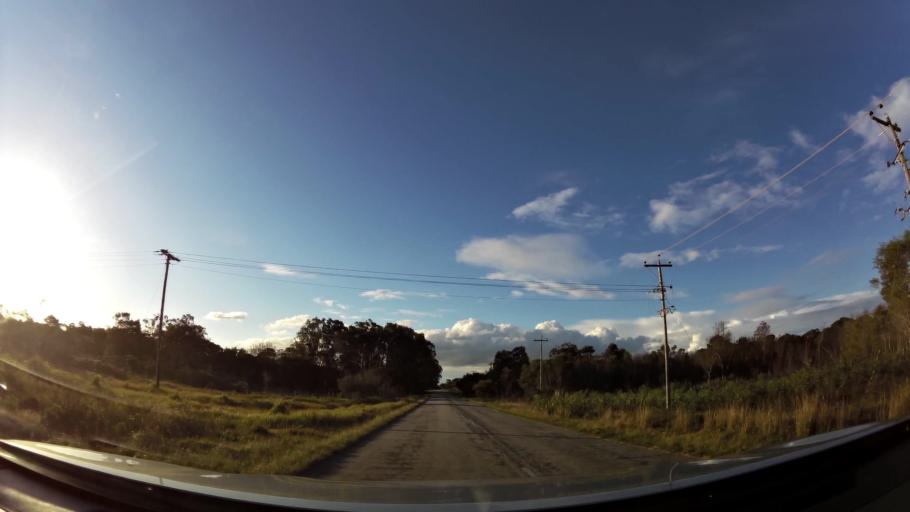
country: ZA
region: Eastern Cape
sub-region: Nelson Mandela Bay Metropolitan Municipality
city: Port Elizabeth
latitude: -33.9825
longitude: 25.4840
